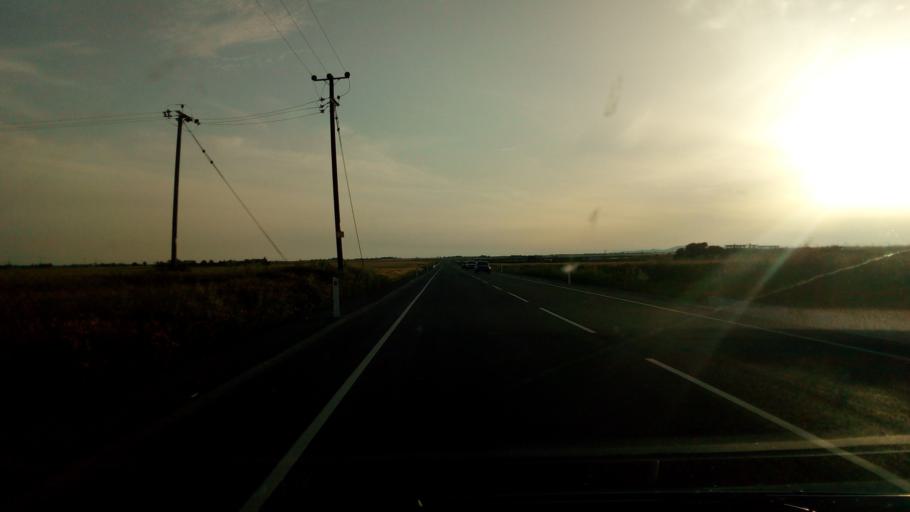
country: CY
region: Larnaka
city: Tersefanou
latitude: 34.8328
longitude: 33.5471
